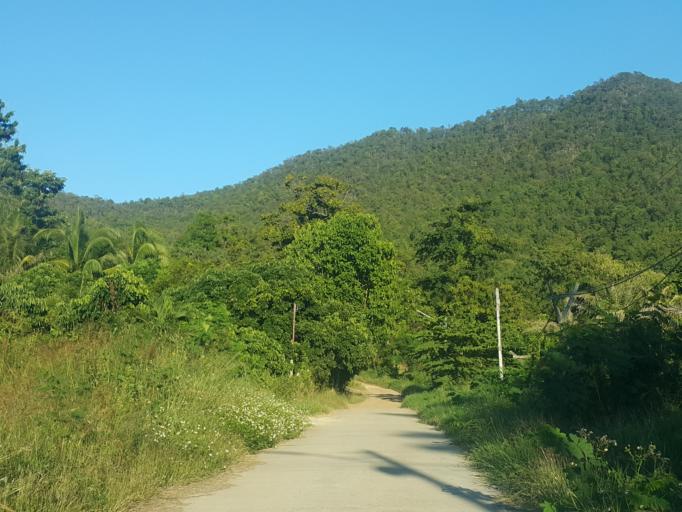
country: TH
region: Chiang Mai
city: San Sai
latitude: 18.9294
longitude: 99.1433
